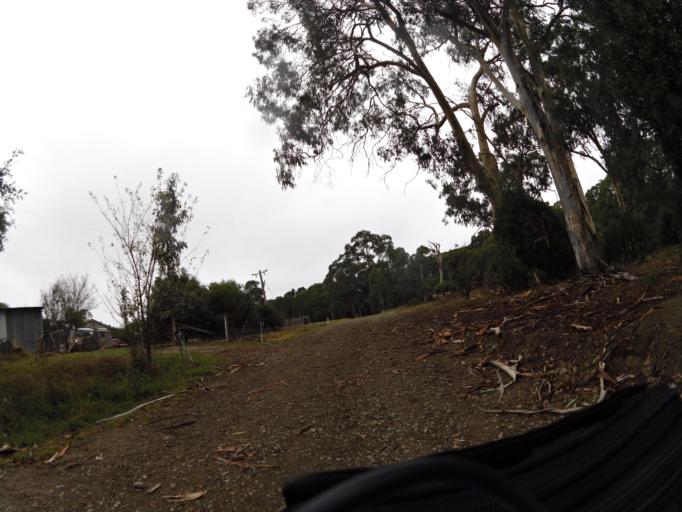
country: AU
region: New South Wales
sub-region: Greater Hume Shire
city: Holbrook
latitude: -36.1711
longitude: 147.4967
